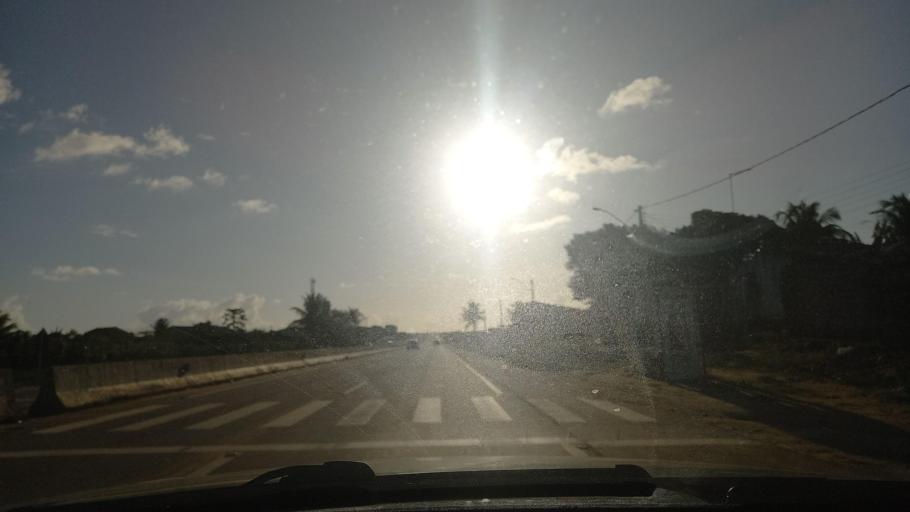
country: BR
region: Alagoas
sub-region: Campo Alegre
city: Campo Alegre
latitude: -9.8028
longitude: -36.2731
